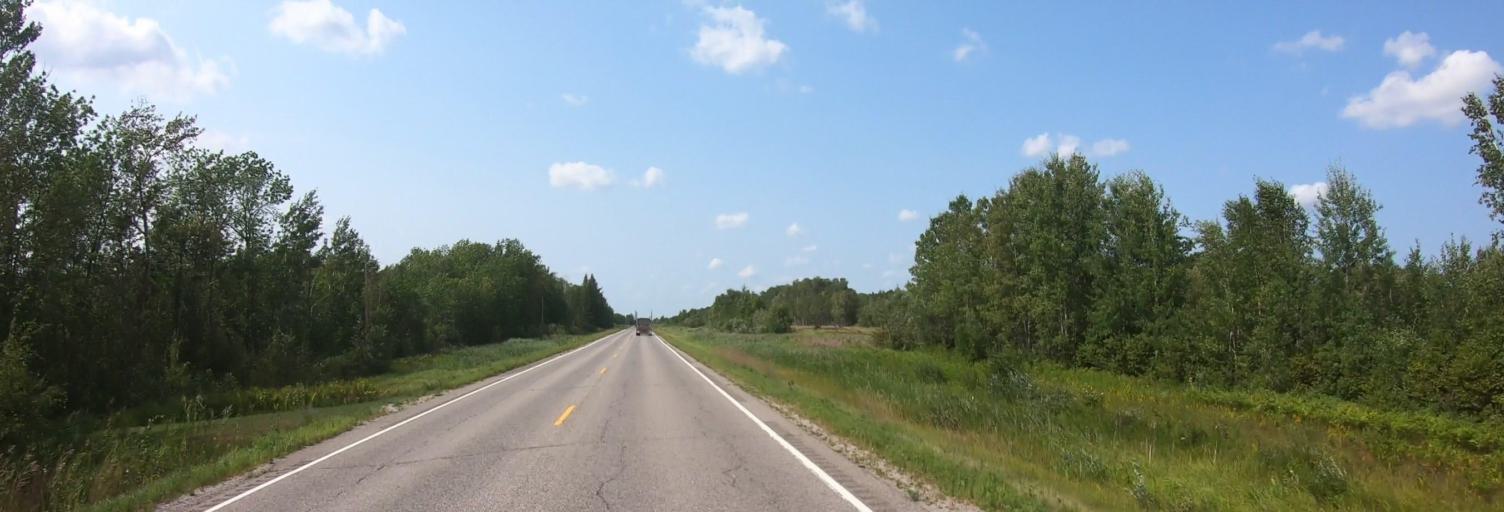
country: US
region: Minnesota
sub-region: Roseau County
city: Warroad
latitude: 48.8135
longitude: -95.1246
